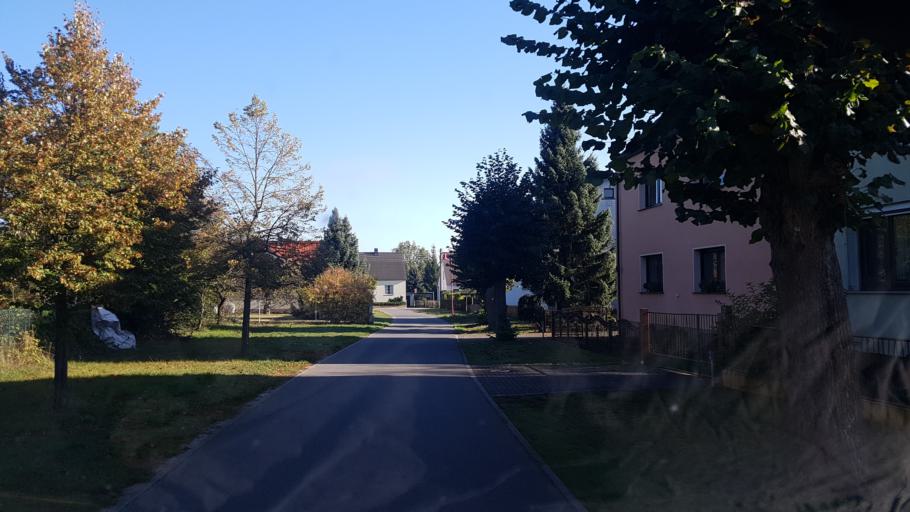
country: DE
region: Brandenburg
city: Hohenleipisch
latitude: 51.4963
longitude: 13.5664
